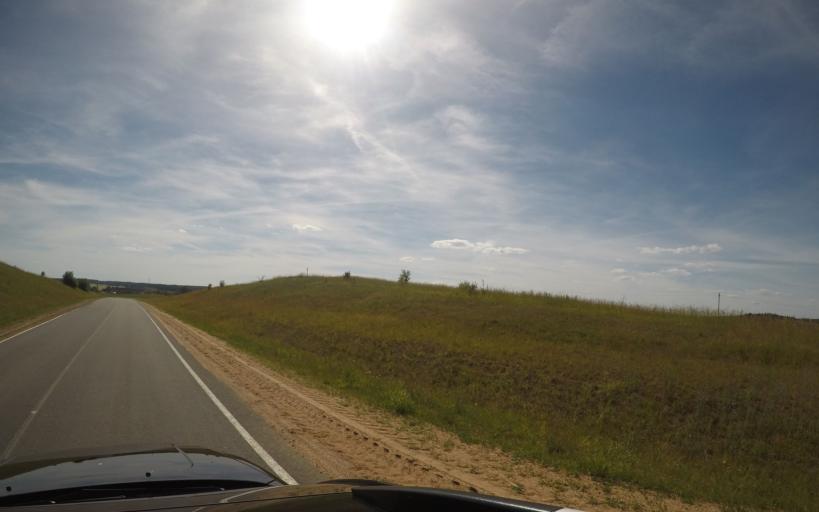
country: BY
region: Grodnenskaya
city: Hal'shany
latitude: 54.2646
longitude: 26.0256
